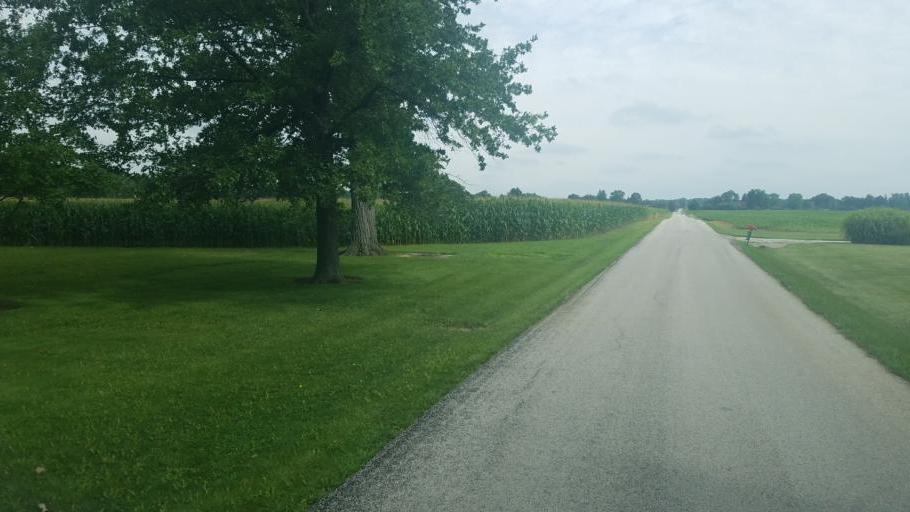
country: US
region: Ohio
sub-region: Morrow County
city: Cardington
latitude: 40.4970
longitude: -82.9391
